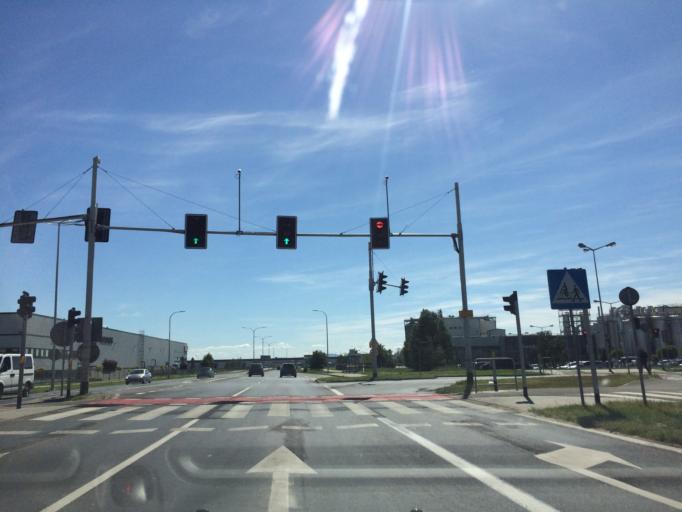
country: PL
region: Lower Silesian Voivodeship
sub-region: Powiat wroclawski
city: Bielany Wroclawskie
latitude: 51.0448
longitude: 16.9535
